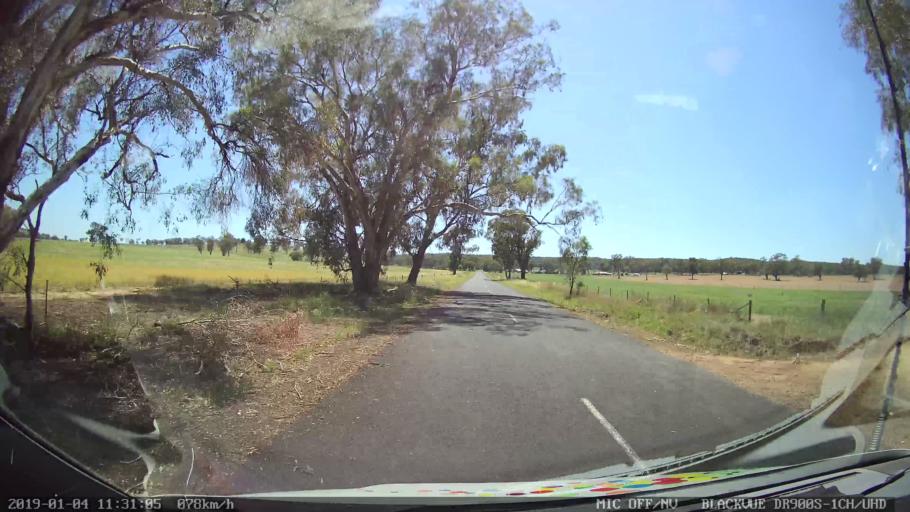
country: AU
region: New South Wales
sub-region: Cabonne
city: Molong
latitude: -33.0740
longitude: 148.7889
